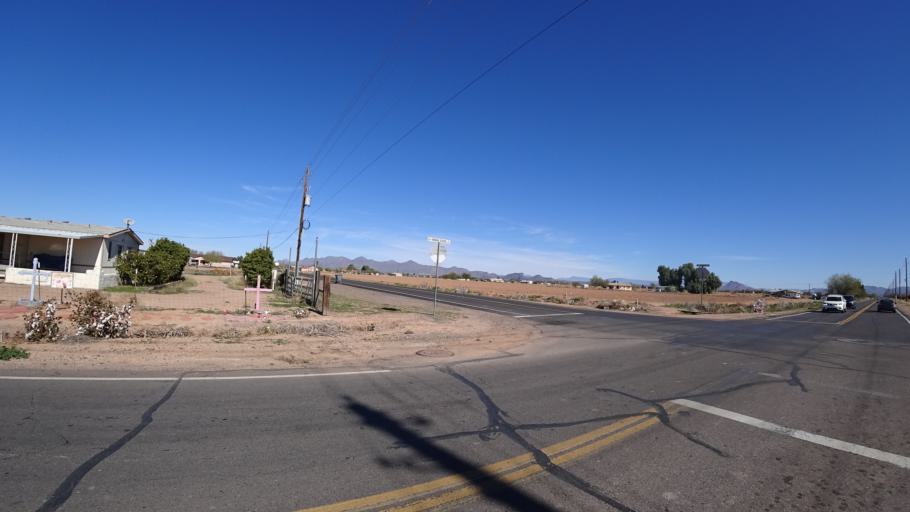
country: US
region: Arizona
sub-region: Maricopa County
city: Scottsdale
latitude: 33.4950
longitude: -111.8656
